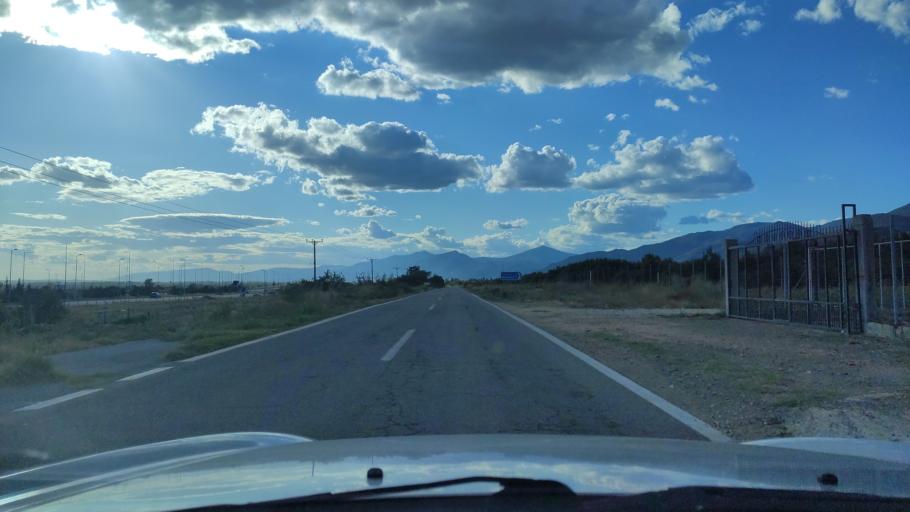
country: GR
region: East Macedonia and Thrace
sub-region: Nomos Xanthis
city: Selero
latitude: 41.1212
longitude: 25.0797
